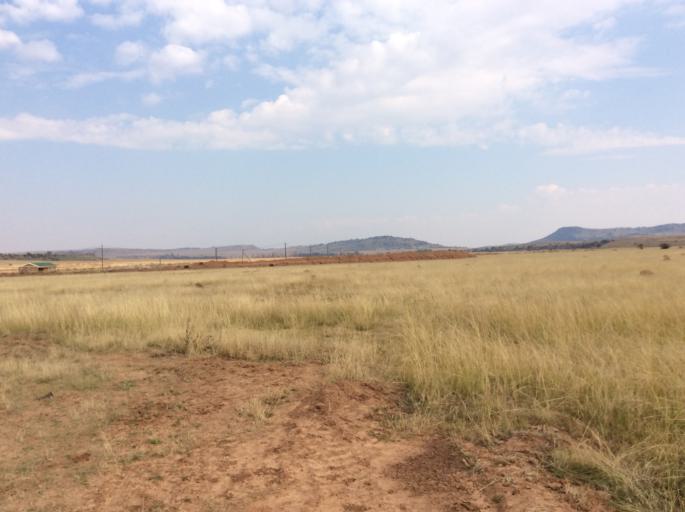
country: LS
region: Mafeteng
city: Mafeteng
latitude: -29.9883
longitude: 26.9976
